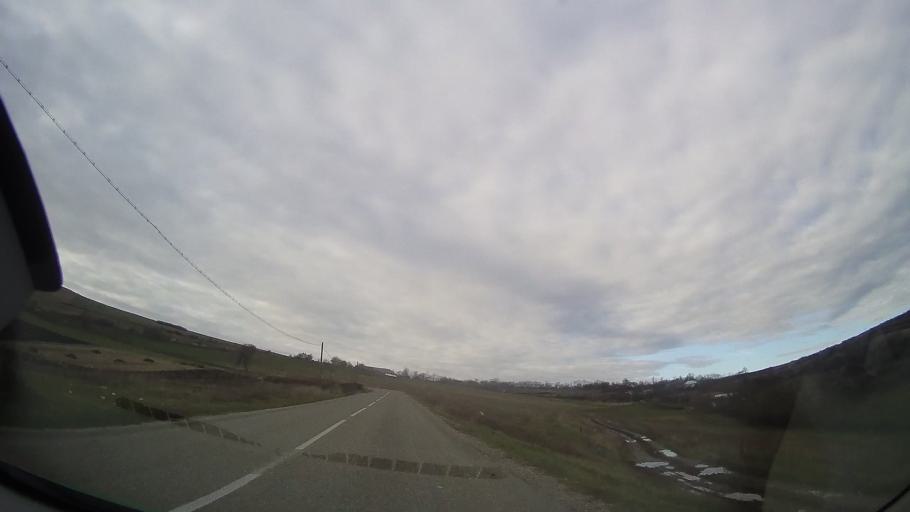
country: RO
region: Bistrita-Nasaud
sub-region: Comuna Budesti
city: Budesti
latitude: 46.8928
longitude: 24.2544
